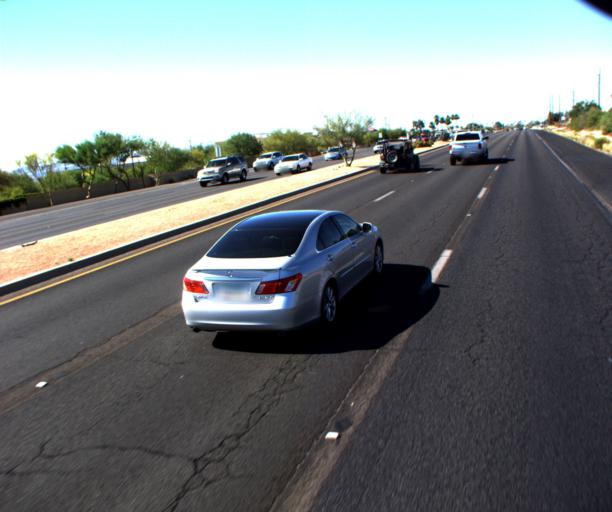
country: US
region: Arizona
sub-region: Pima County
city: Casas Adobes
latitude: 32.3476
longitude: -110.9756
